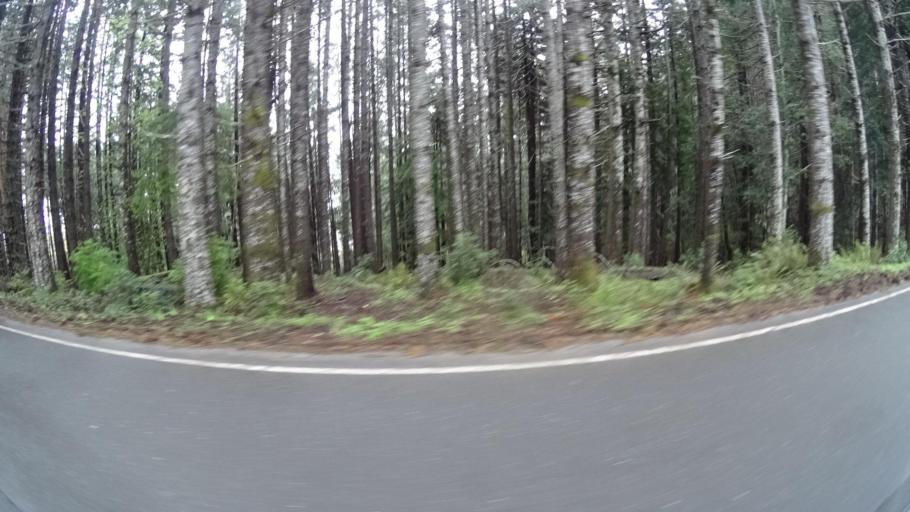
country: US
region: California
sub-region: Humboldt County
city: Westhaven-Moonstone
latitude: 41.1893
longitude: -123.9313
